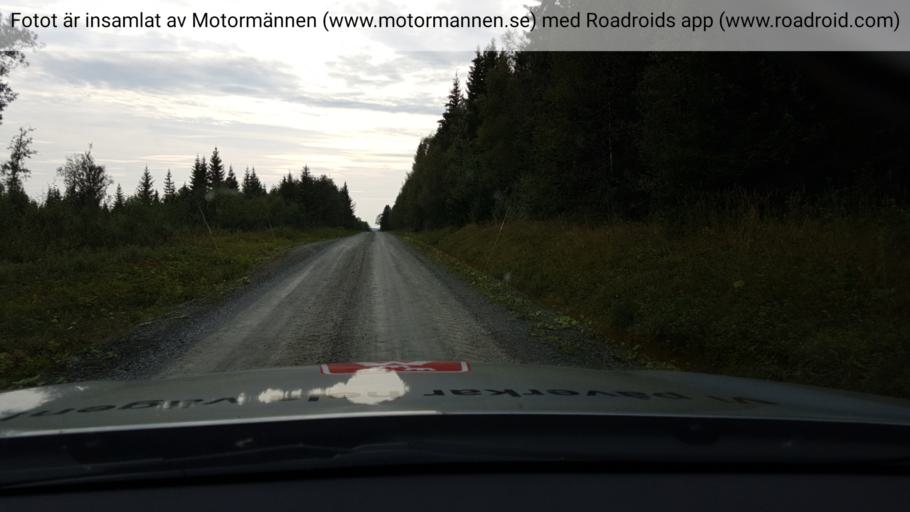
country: SE
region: Jaemtland
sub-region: Krokoms Kommun
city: Valla
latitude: 63.5747
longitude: 13.9369
